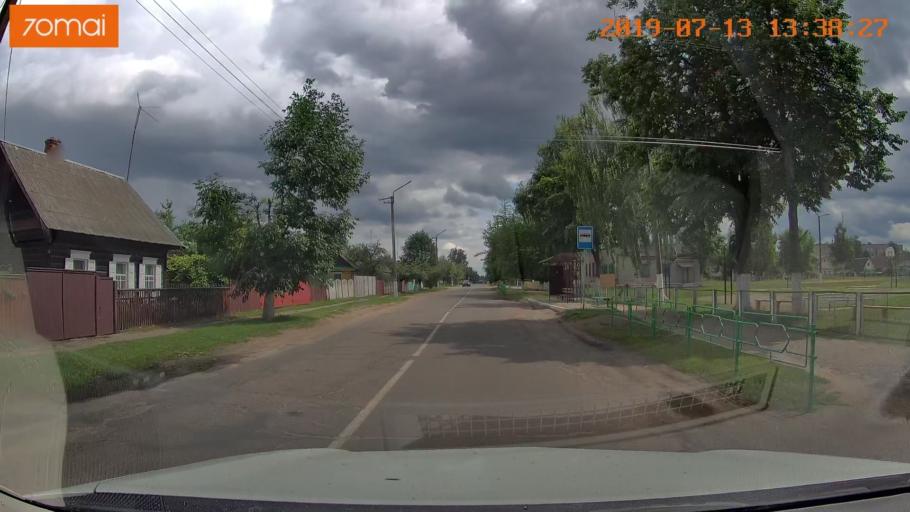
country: BY
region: Mogilev
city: Asipovichy
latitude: 53.2981
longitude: 28.6345
